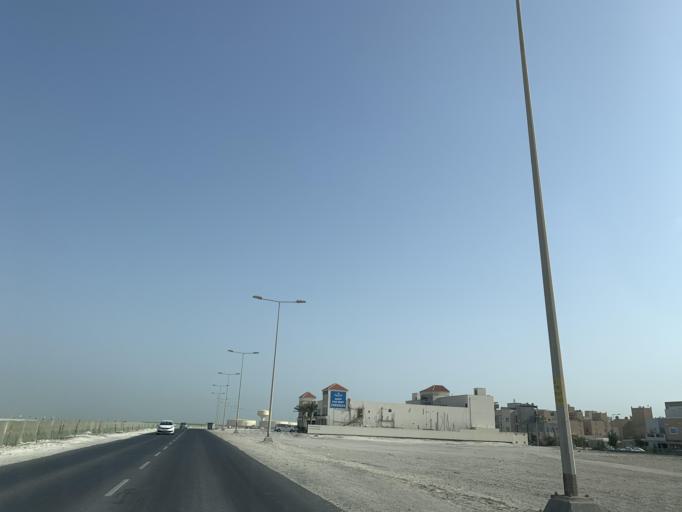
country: BH
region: Muharraq
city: Al Muharraq
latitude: 26.2744
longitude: 50.5944
